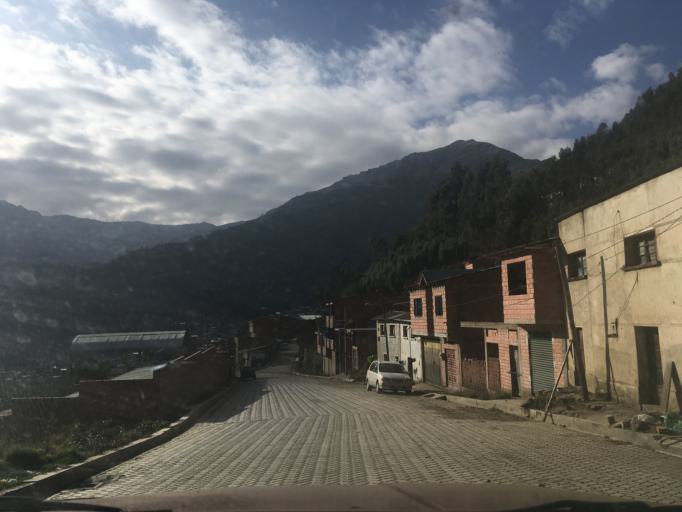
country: BO
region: La Paz
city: Quime
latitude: -16.9794
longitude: -67.2235
